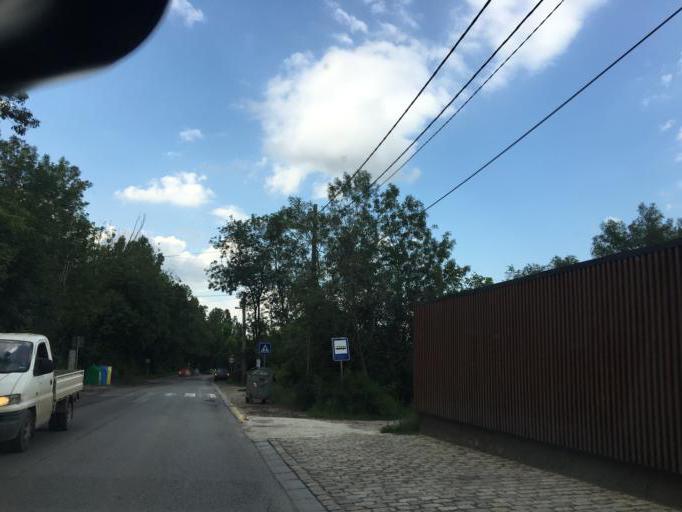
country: BG
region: Sofia-Capital
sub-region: Stolichna Obshtina
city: Sofia
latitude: 42.6318
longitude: 23.3550
